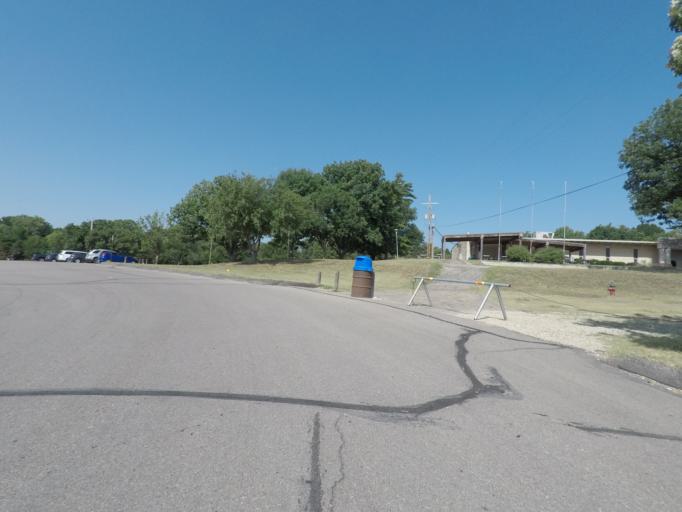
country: US
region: Kansas
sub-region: Riley County
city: Manhattan
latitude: 39.1991
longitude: -96.6210
